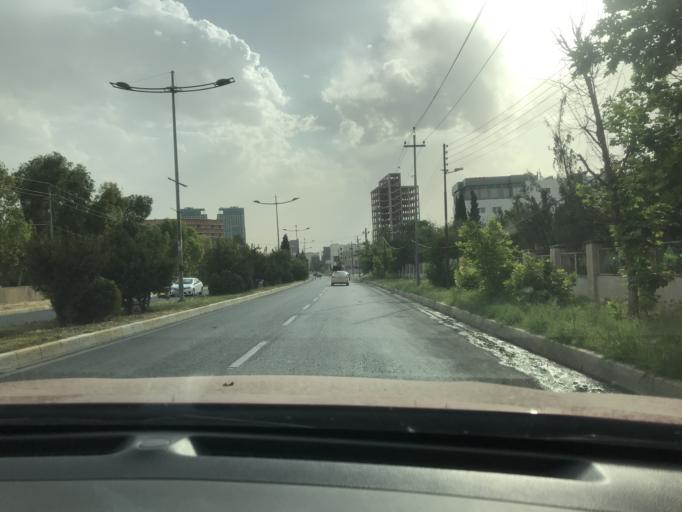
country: IQ
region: Arbil
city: Erbil
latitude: 36.2196
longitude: 44.0129
